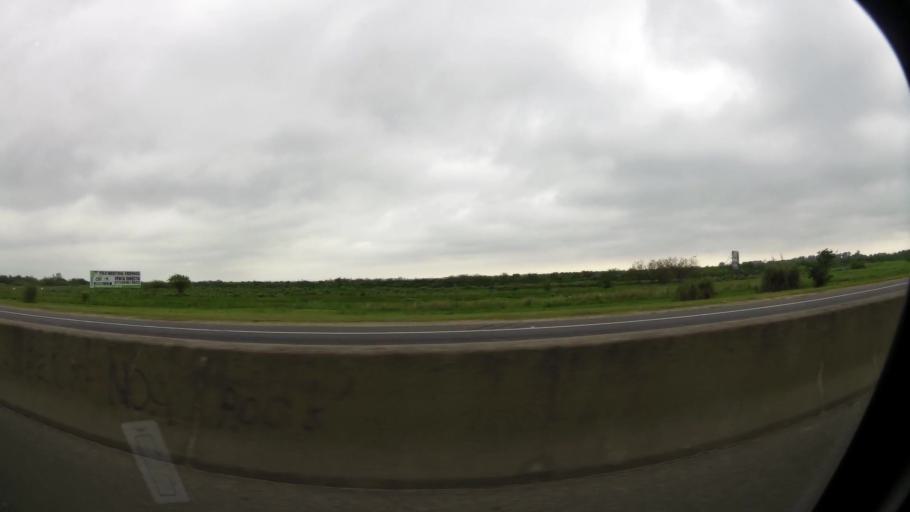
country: AR
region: Buenos Aires
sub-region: Partido de La Plata
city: La Plata
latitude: -34.8716
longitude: -57.9836
